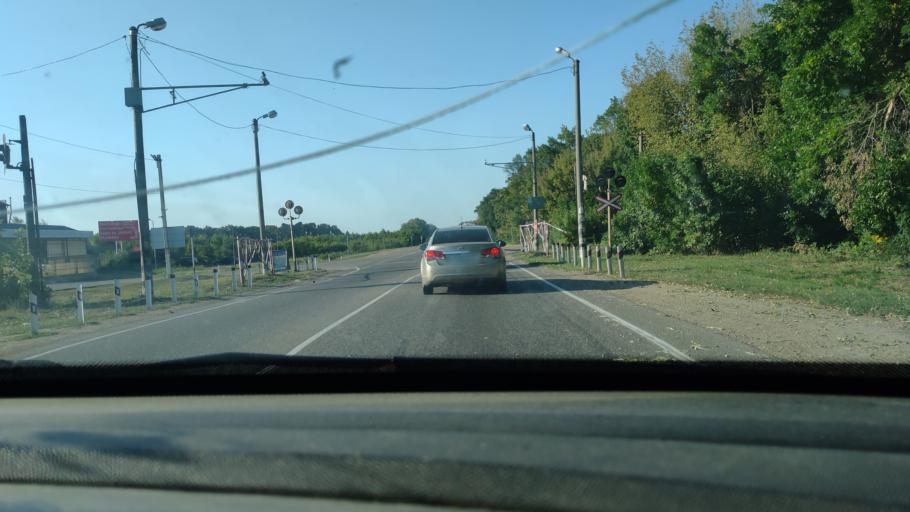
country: RU
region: Krasnodarskiy
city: Medvedovskaya
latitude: 45.4480
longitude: 38.9928
